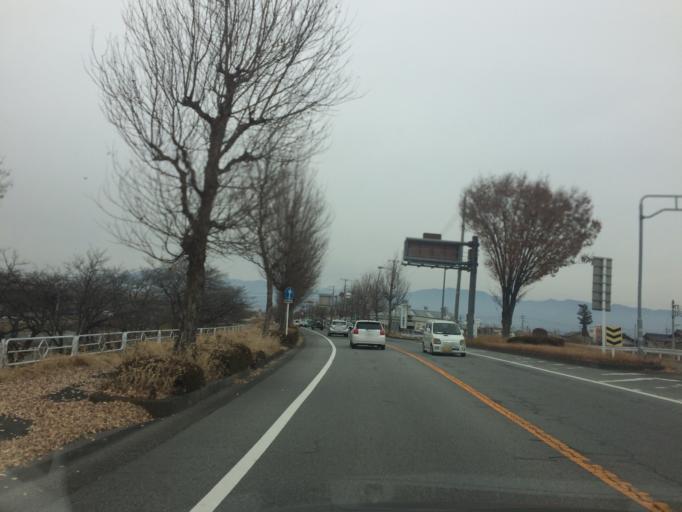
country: JP
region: Yamanashi
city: Ryuo
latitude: 35.6075
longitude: 138.5176
